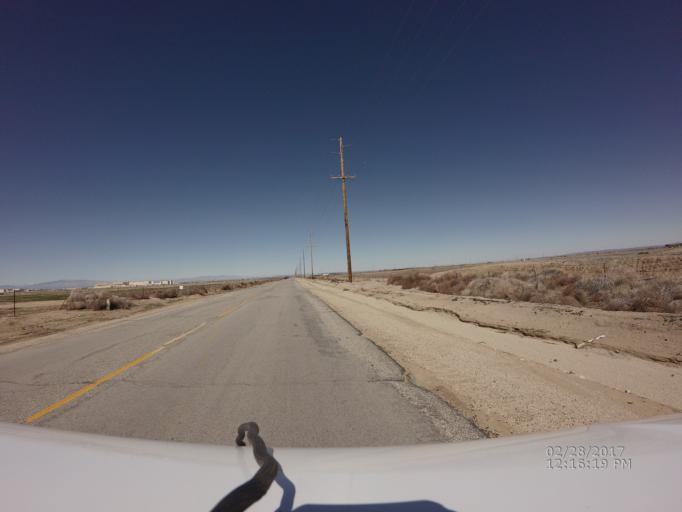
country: US
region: California
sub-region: Los Angeles County
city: Palmdale
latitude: 34.6240
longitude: -118.0587
